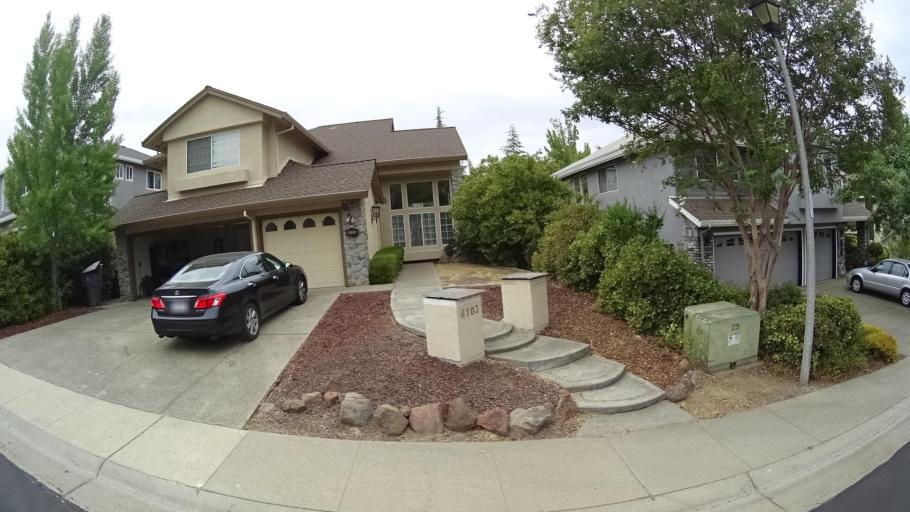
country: US
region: California
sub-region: Placer County
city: Rocklin
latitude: 38.7909
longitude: -121.2647
